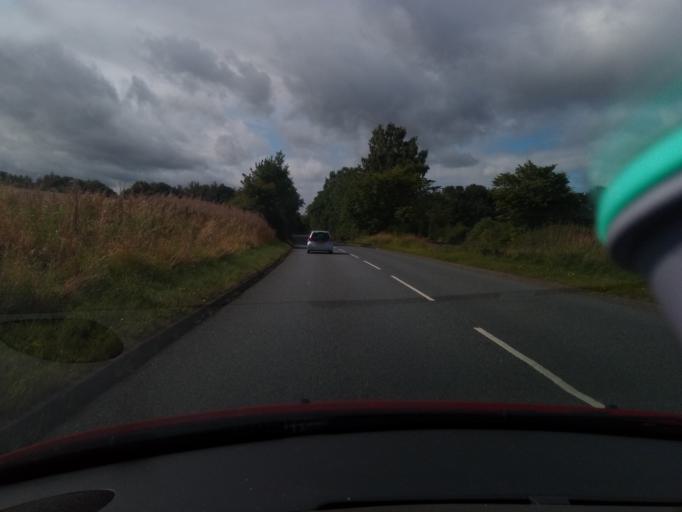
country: GB
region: Scotland
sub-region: The Scottish Borders
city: Saint Boswells
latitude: 55.5706
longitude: -2.5788
